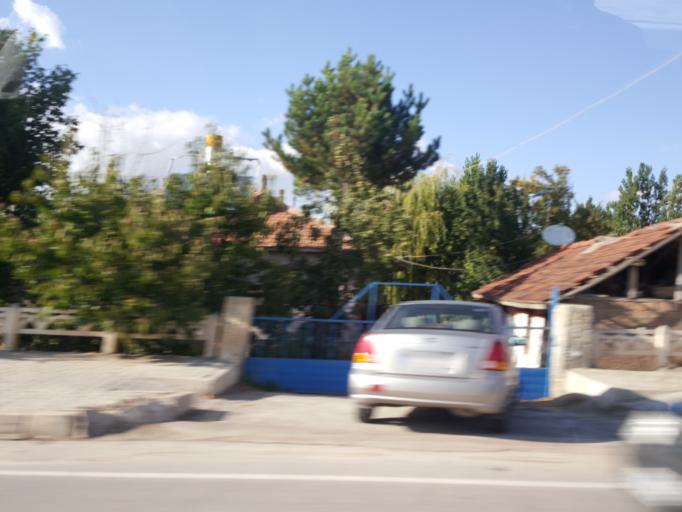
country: TR
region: Tokat
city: Yesilyurt
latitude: 40.0093
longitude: 36.2197
